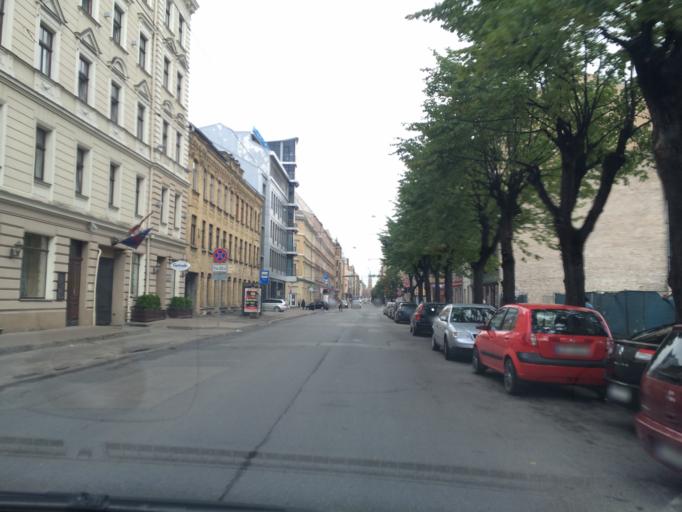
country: LV
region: Riga
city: Riga
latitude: 56.9504
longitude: 24.1352
